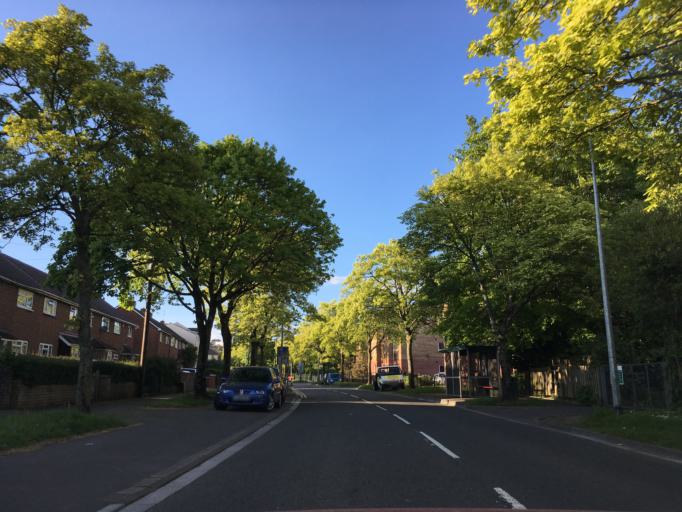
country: GB
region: Wales
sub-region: Newport
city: Marshfield
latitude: 51.5064
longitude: -3.1200
